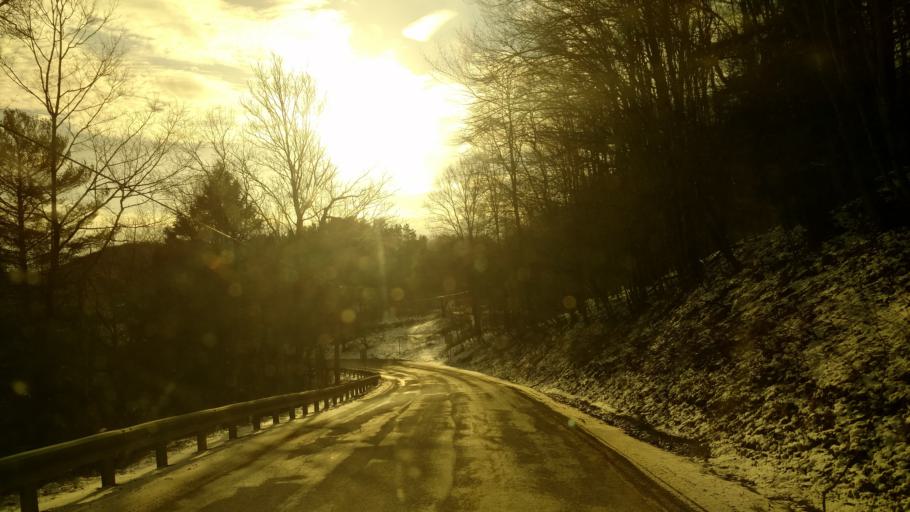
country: US
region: New York
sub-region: Allegany County
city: Andover
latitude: 41.9454
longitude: -77.8229
